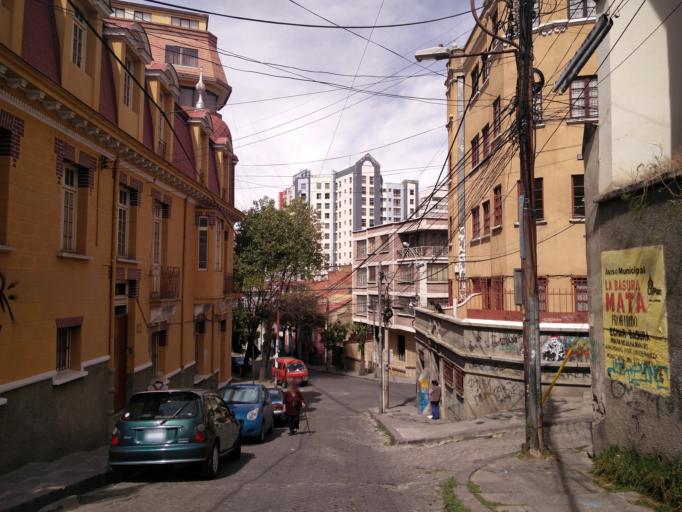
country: BO
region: La Paz
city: La Paz
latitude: -16.5087
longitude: -68.1310
